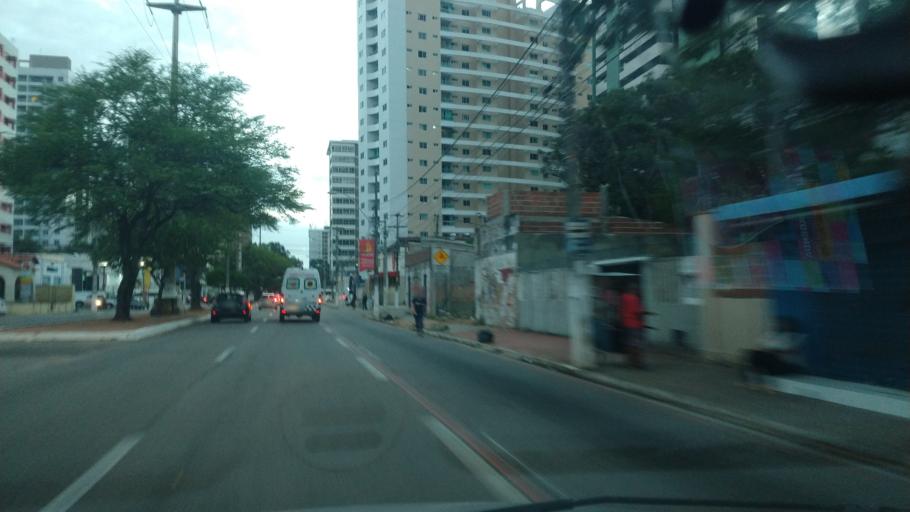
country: BR
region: Rio Grande do Norte
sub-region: Natal
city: Natal
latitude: -5.7856
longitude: -35.2005
